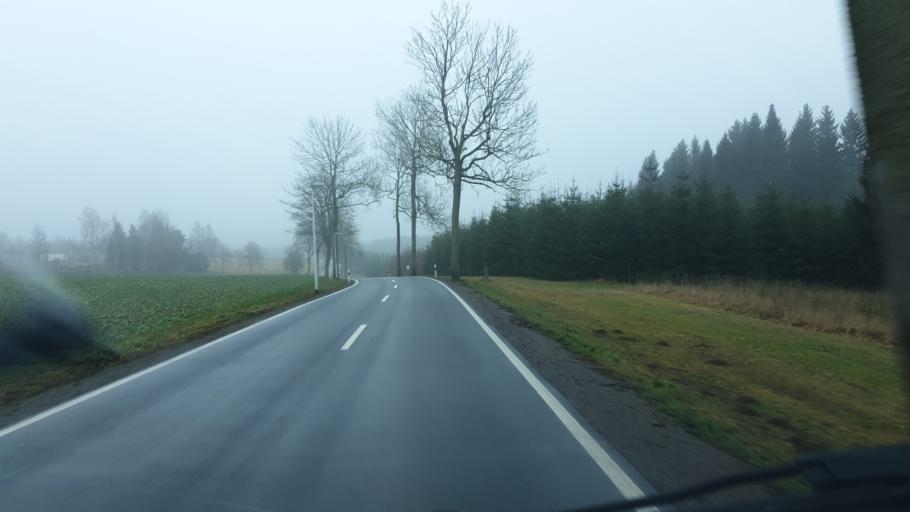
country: DE
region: Saxony
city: Sayda
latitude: 50.7056
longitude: 13.4339
